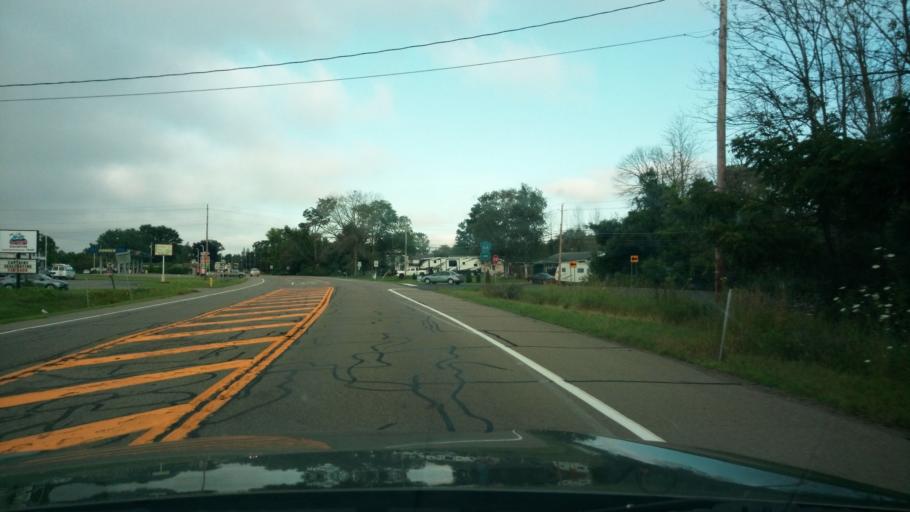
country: US
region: New York
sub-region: Chemung County
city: Big Flats
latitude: 42.1335
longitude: -76.9428
